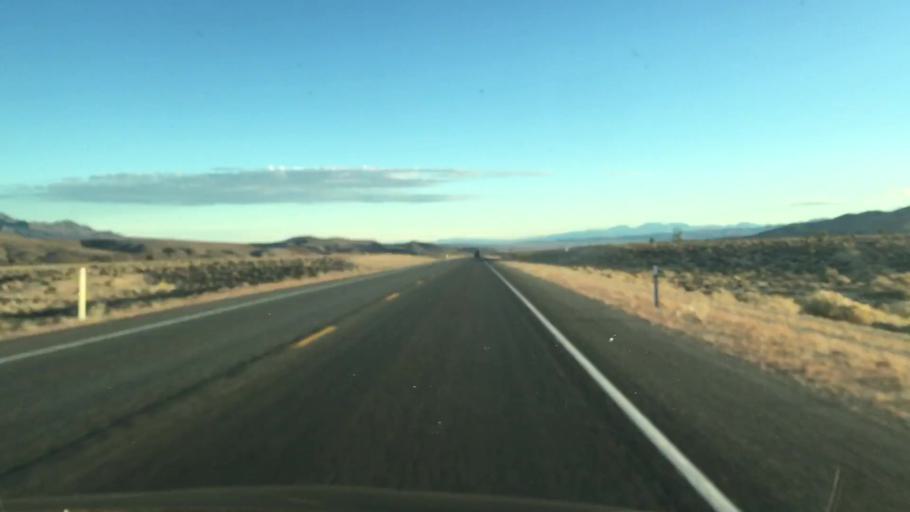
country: US
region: Nevada
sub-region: Esmeralda County
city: Goldfield
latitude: 37.5910
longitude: -117.2088
